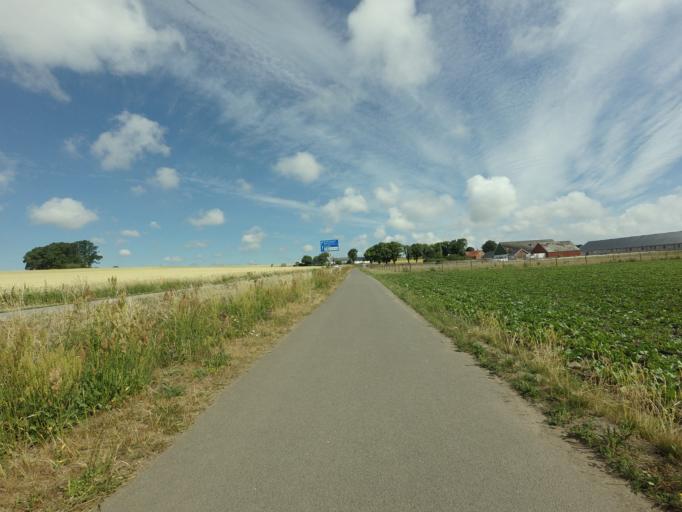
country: SE
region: Skane
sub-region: Simrishamns Kommun
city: Simrishamn
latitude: 55.4817
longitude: 14.2847
